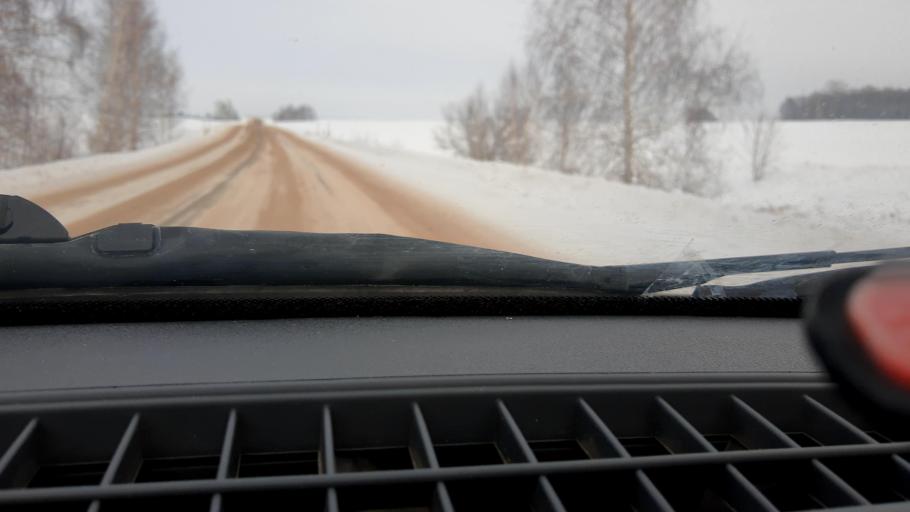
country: RU
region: Bashkortostan
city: Alekseyevka
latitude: 54.6150
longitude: 54.9551
